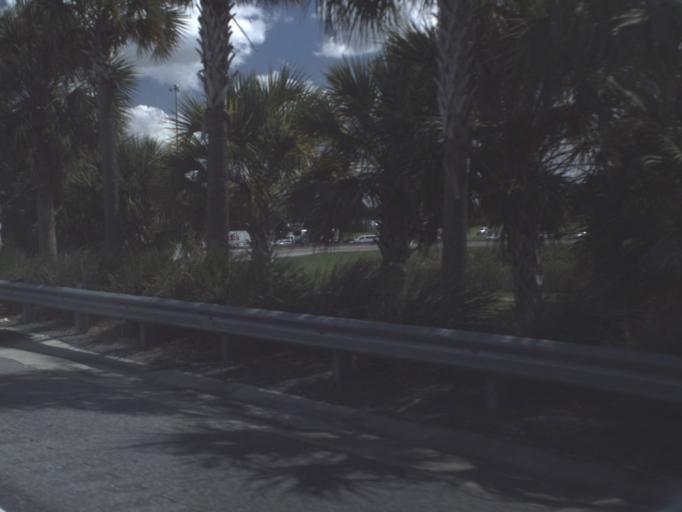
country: US
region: Florida
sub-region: Orange County
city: Sky Lake
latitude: 28.4337
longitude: -81.4067
